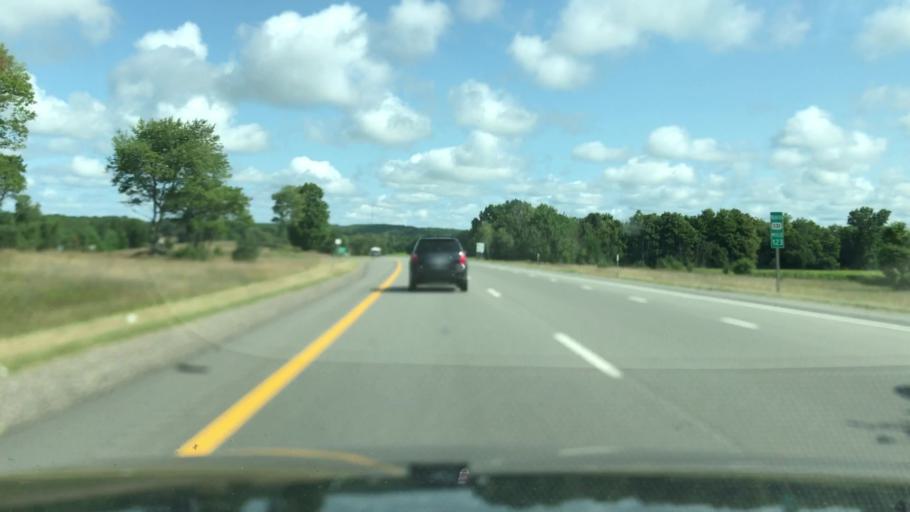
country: US
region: Michigan
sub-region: Montcalm County
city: Howard City
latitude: 43.4655
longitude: -85.4760
